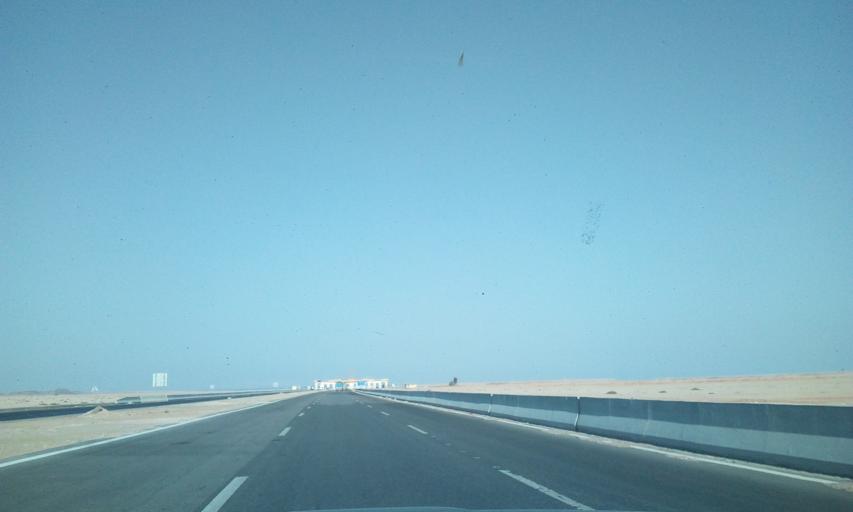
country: EG
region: As Suways
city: Ain Sukhna
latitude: 29.1100
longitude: 32.5409
